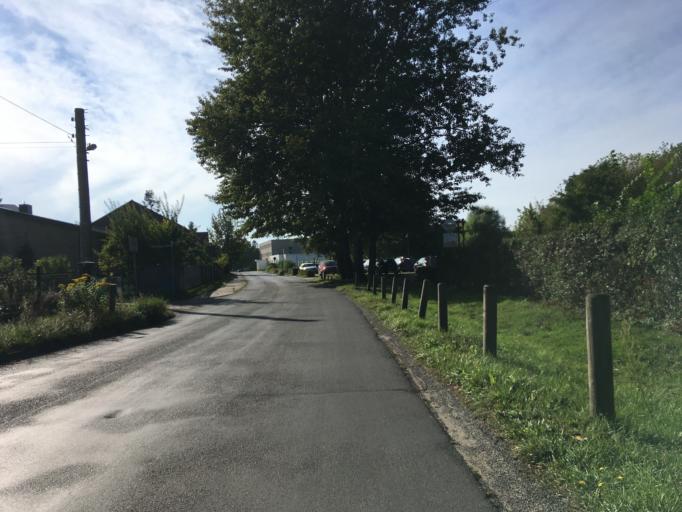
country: DE
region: Brandenburg
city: Neuenhagen
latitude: 52.5205
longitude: 13.7133
